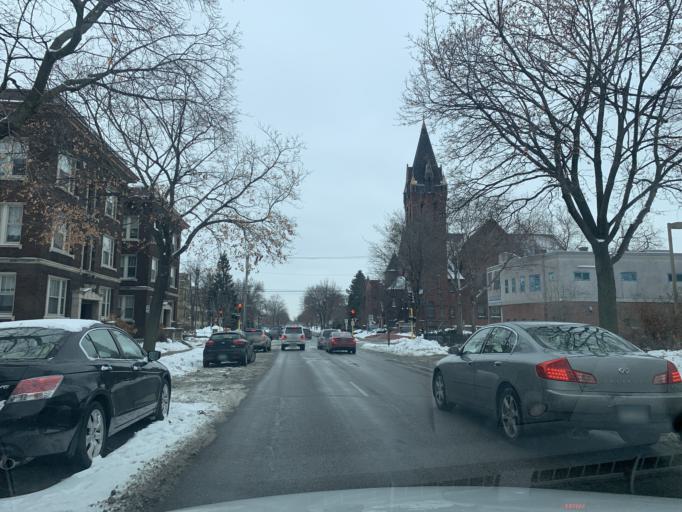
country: US
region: Minnesota
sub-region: Hennepin County
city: Minneapolis
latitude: 44.9561
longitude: -93.2796
